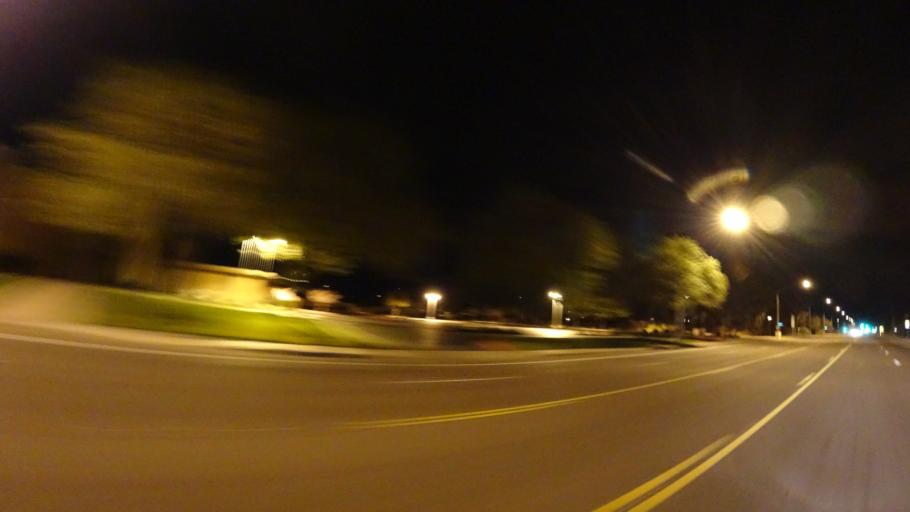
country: US
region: Arizona
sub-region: Pinal County
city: Apache Junction
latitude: 33.4369
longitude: -111.6810
